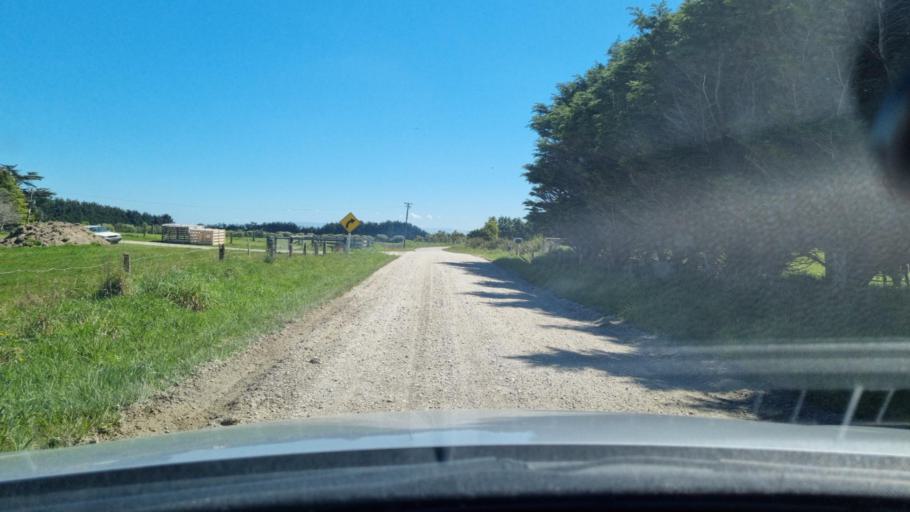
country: NZ
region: Southland
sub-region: Invercargill City
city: Invercargill
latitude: -46.4162
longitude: 168.2652
